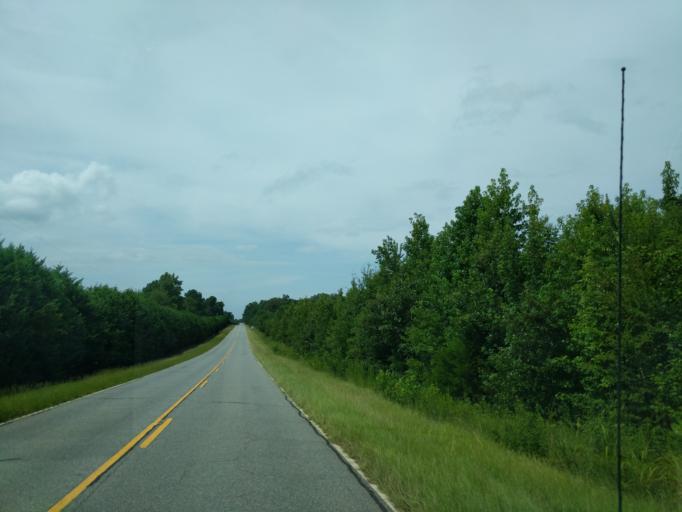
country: US
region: South Carolina
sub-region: Abbeville County
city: Calhoun Falls
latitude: 34.1553
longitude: -82.5999
